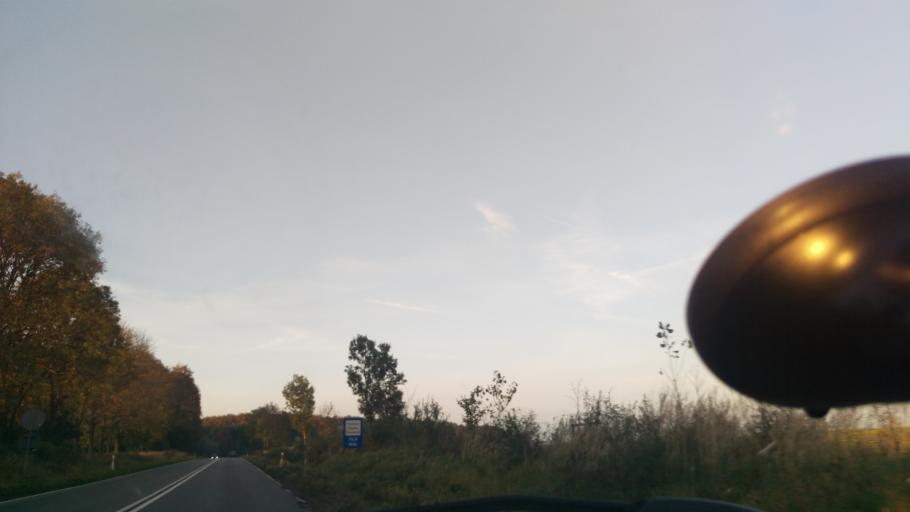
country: PL
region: West Pomeranian Voivodeship
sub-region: Powiat gryfinski
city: Stare Czarnowo
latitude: 53.3085
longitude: 14.7926
